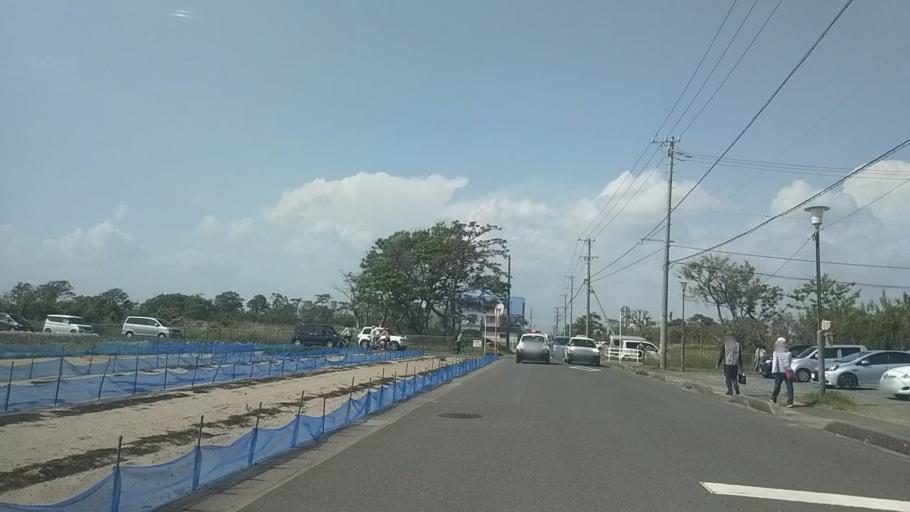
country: JP
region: Shizuoka
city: Hamamatsu
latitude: 34.6671
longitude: 137.7225
